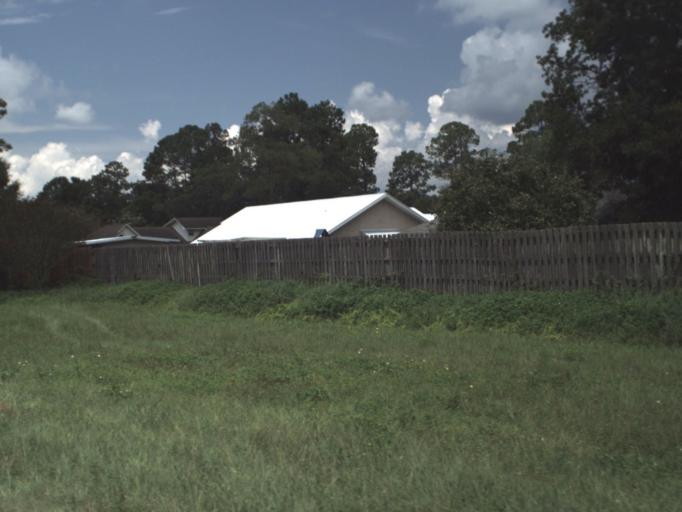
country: US
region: Florida
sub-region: Bay County
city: Lynn Haven
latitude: 30.2333
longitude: -85.6170
